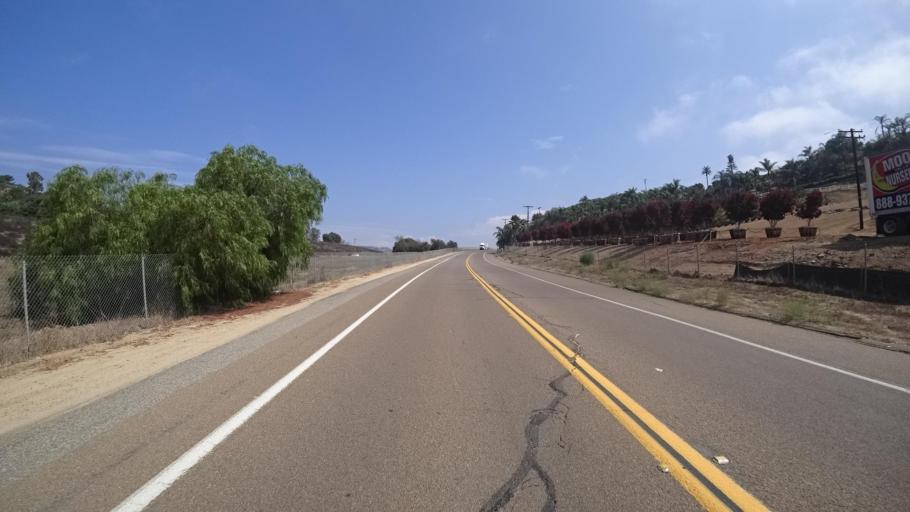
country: US
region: California
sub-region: San Diego County
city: Rainbow
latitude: 33.3979
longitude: -117.1707
